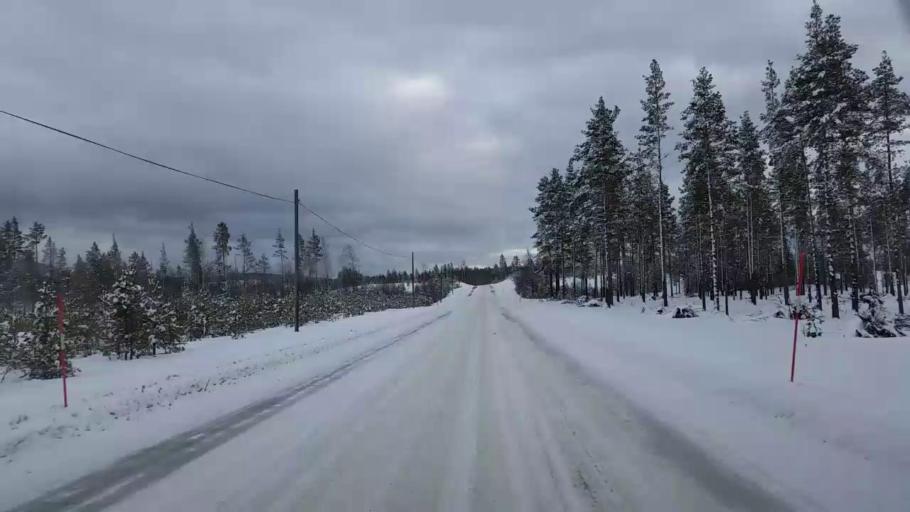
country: SE
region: Jaemtland
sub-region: Harjedalens Kommun
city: Sveg
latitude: 62.1271
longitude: 14.9804
